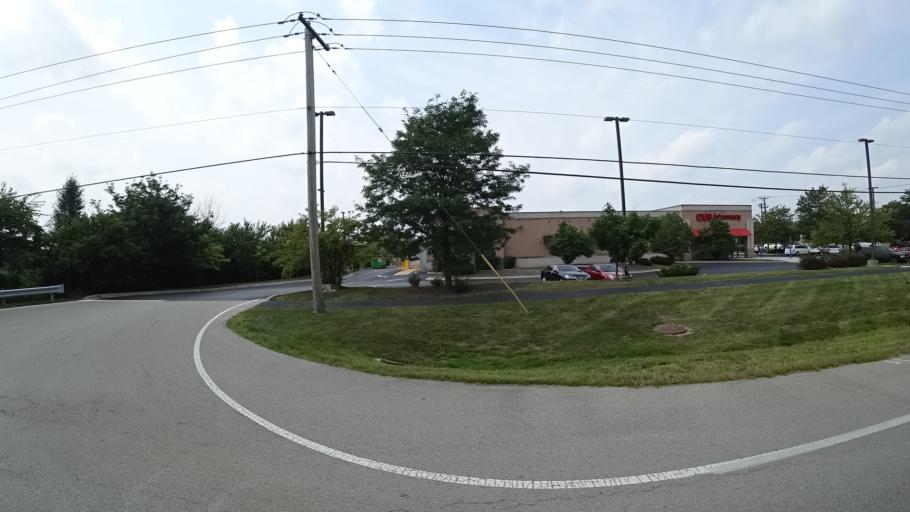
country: US
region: Illinois
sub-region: Will County
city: Goodings Grove
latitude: 41.6291
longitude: -87.8925
